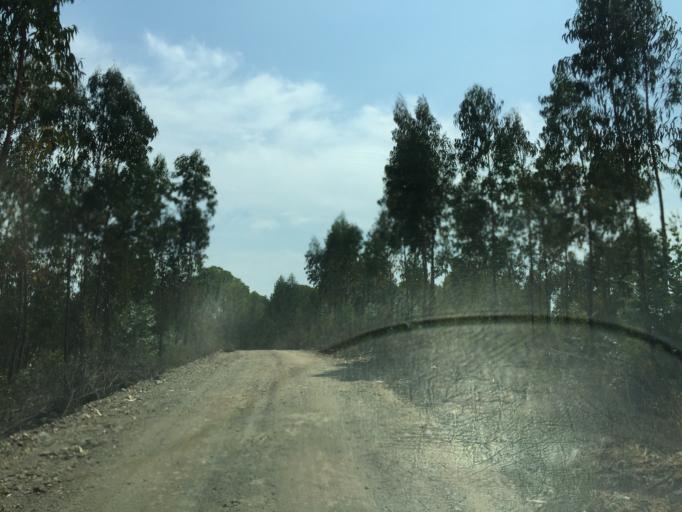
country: PT
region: Setubal
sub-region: Grandola
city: Grandola
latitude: 38.1084
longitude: -8.4915
